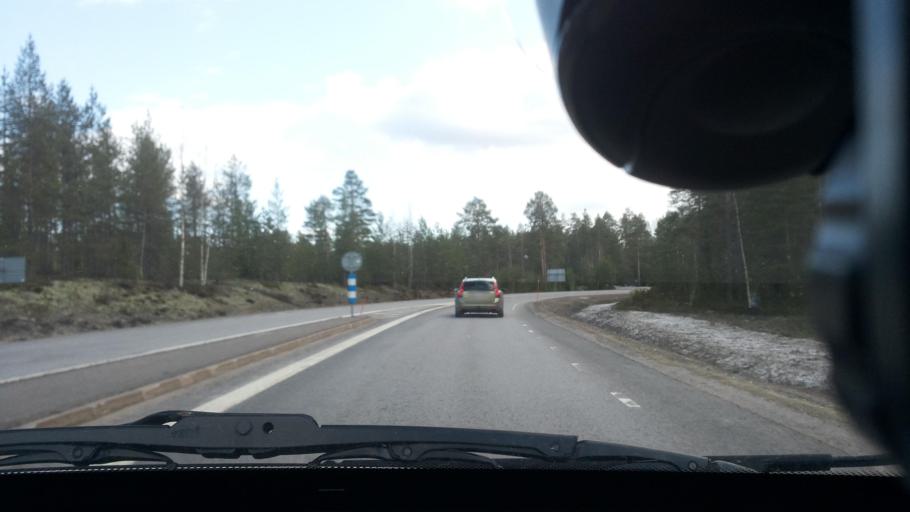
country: SE
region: Norrbotten
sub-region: Lulea Kommun
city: Gammelstad
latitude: 65.5969
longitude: 22.0460
